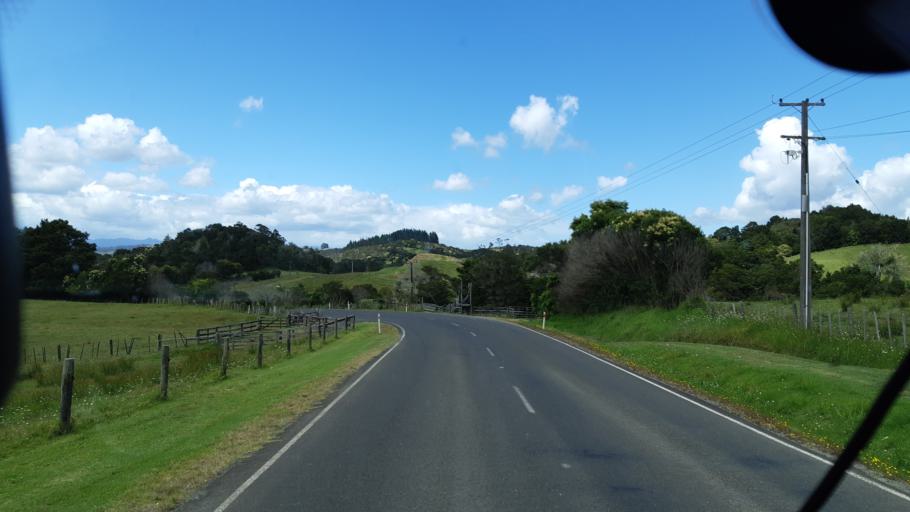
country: NZ
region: Northland
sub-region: Far North District
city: Taipa
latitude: -35.2648
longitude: 173.5244
